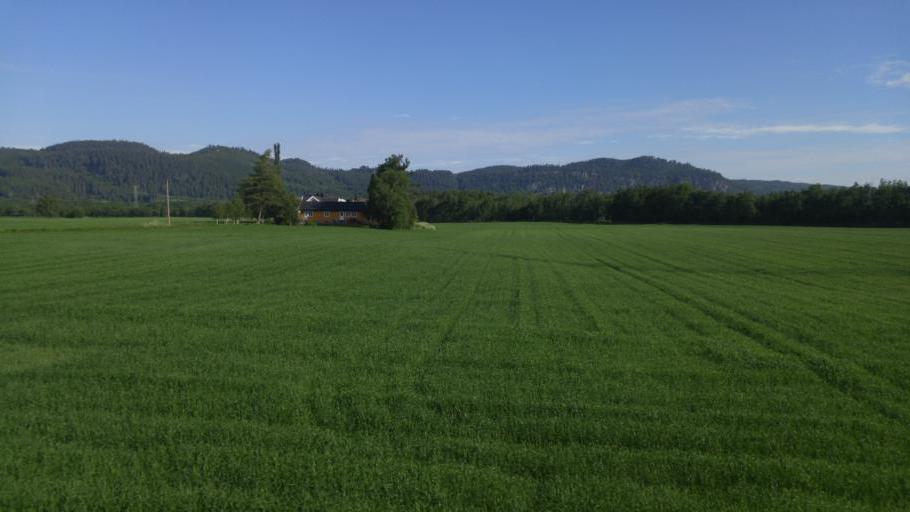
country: NO
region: Nord-Trondelag
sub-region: Stjordal
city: Stjordalshalsen
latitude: 63.4532
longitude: 11.0378
